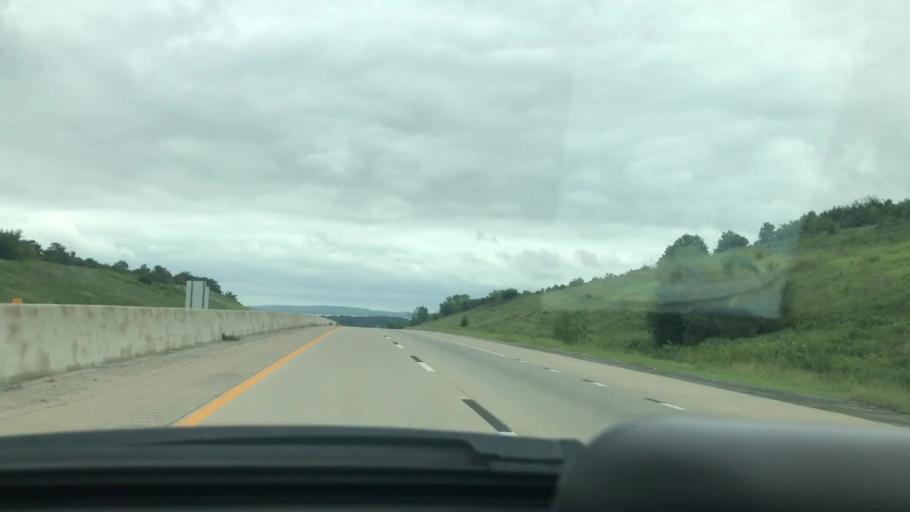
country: US
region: Oklahoma
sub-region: McIntosh County
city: Eufaula
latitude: 35.1763
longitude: -95.6465
